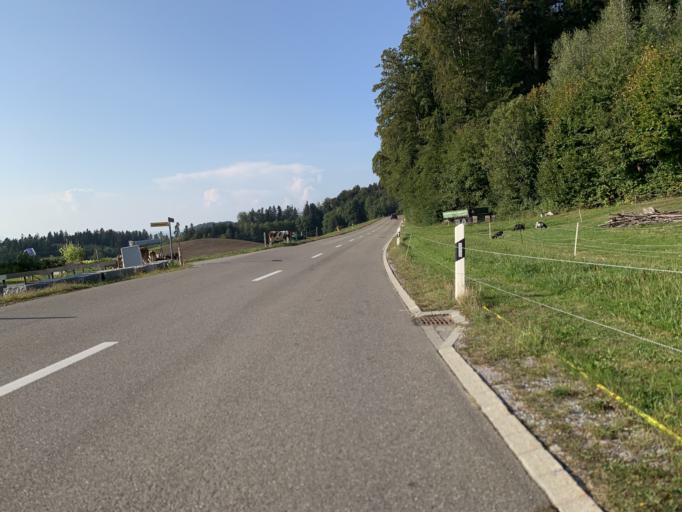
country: CH
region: Zurich
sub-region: Bezirk Hinwil
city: Baretswil
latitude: 47.3227
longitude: 8.8467
